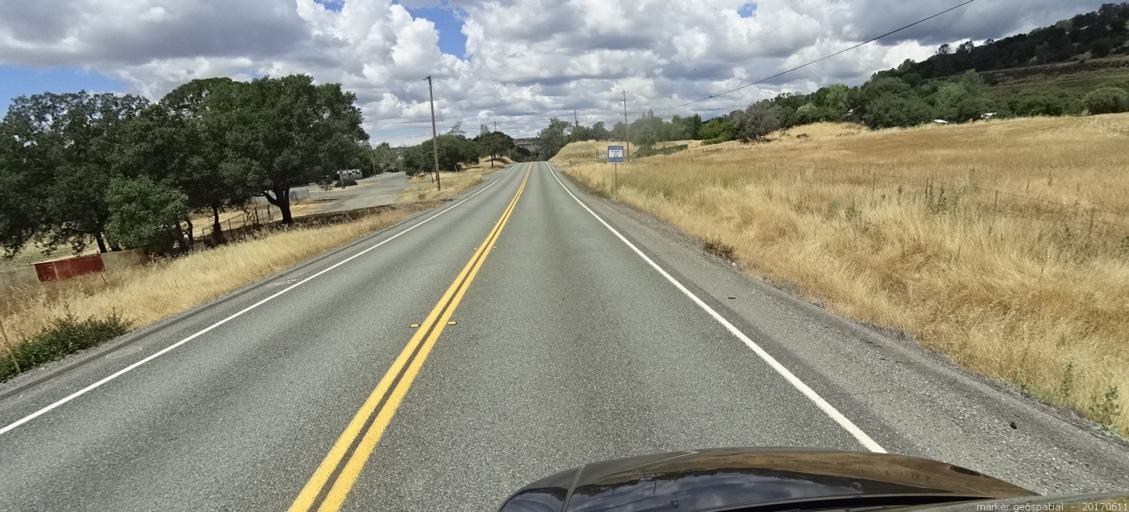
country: US
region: California
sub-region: Butte County
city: Paradise
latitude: 39.6513
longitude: -121.5611
